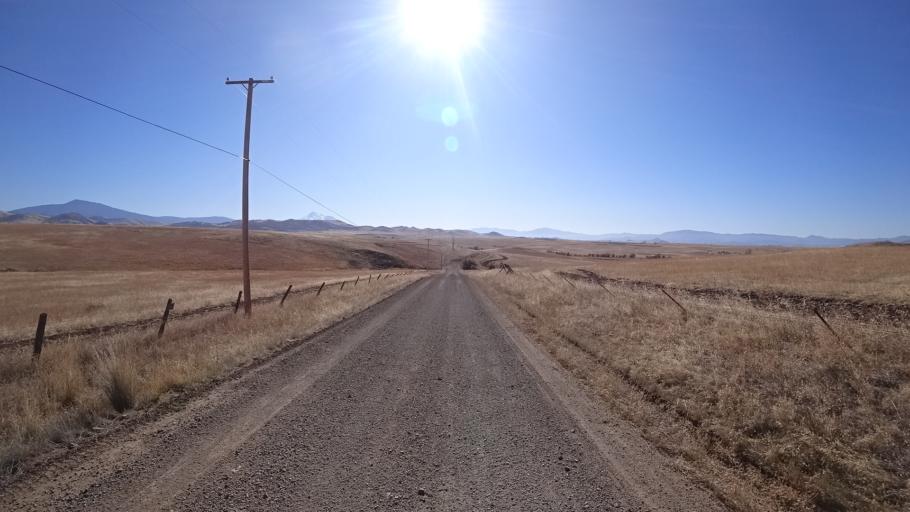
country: US
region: California
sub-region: Siskiyou County
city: Montague
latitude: 41.8341
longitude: -122.4206
